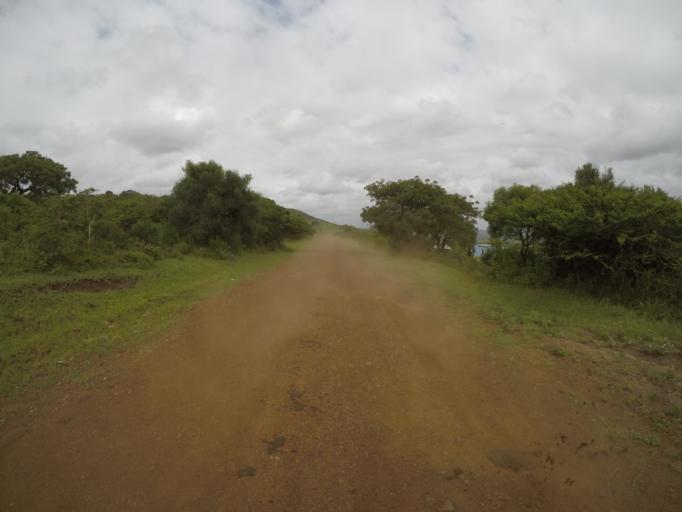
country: ZA
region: KwaZulu-Natal
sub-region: uThungulu District Municipality
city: Empangeni
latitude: -28.6137
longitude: 31.8975
